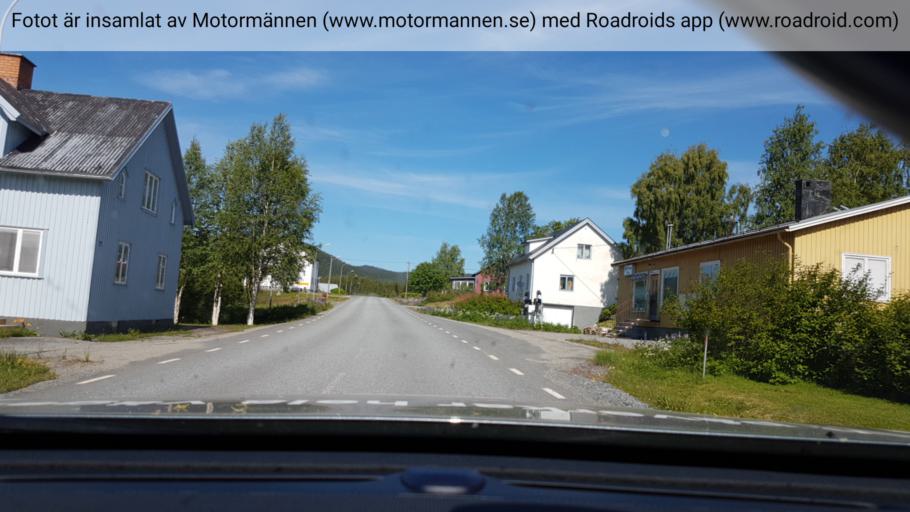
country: SE
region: Vaesterbotten
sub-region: Vilhelmina Kommun
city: Sjoberg
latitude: 64.7056
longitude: 15.5324
